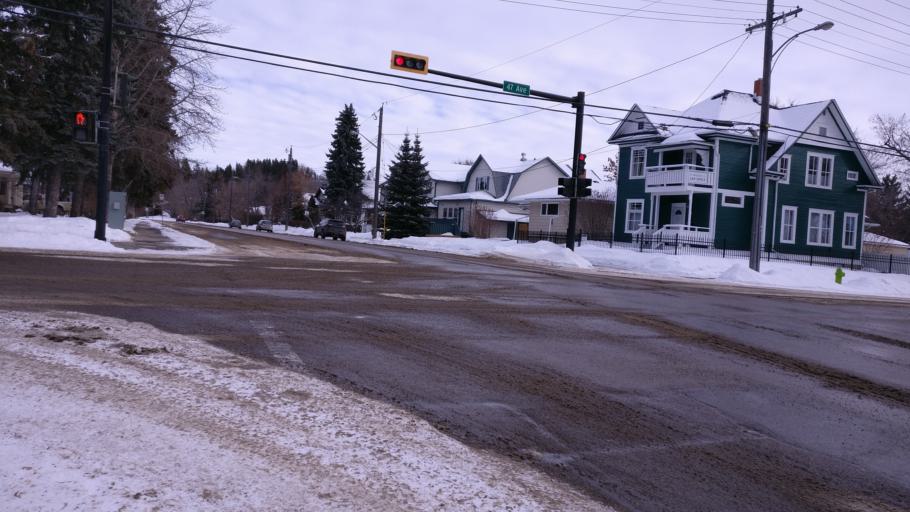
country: CA
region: Alberta
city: Red Deer
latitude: 52.2681
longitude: -113.8052
